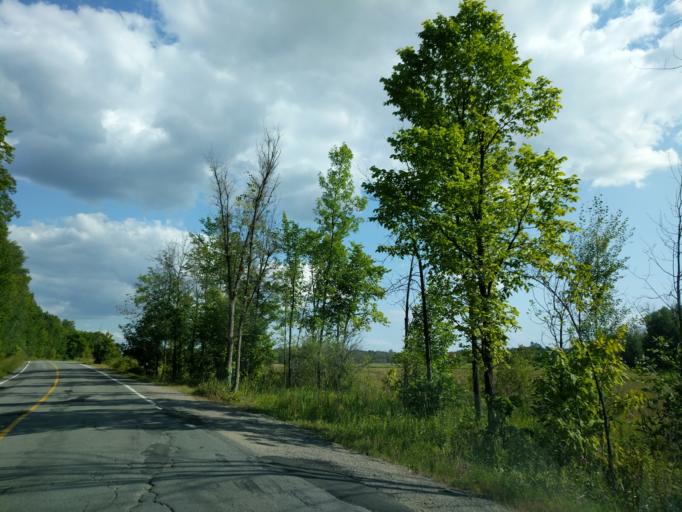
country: CA
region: Quebec
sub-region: Outaouais
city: Gatineau
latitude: 45.4695
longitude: -75.8501
